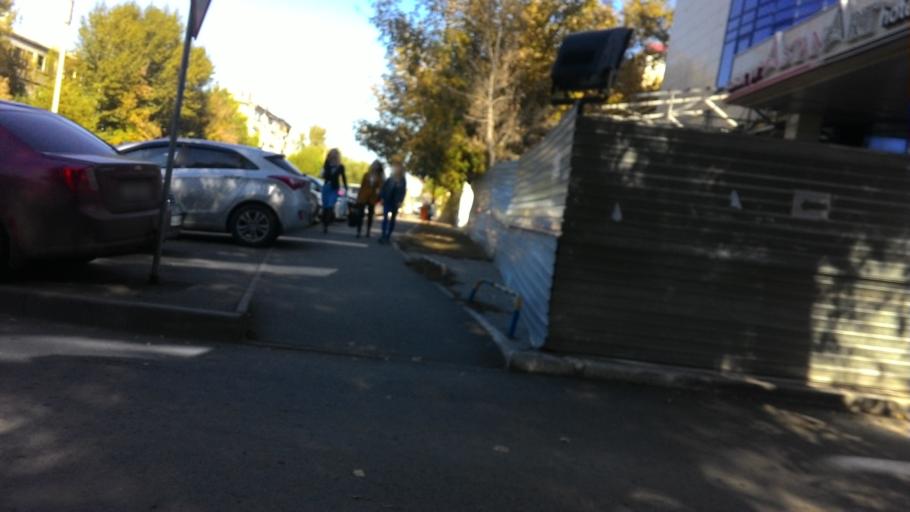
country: KZ
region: Astana Qalasy
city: Astana
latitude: 51.1788
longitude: 71.4129
